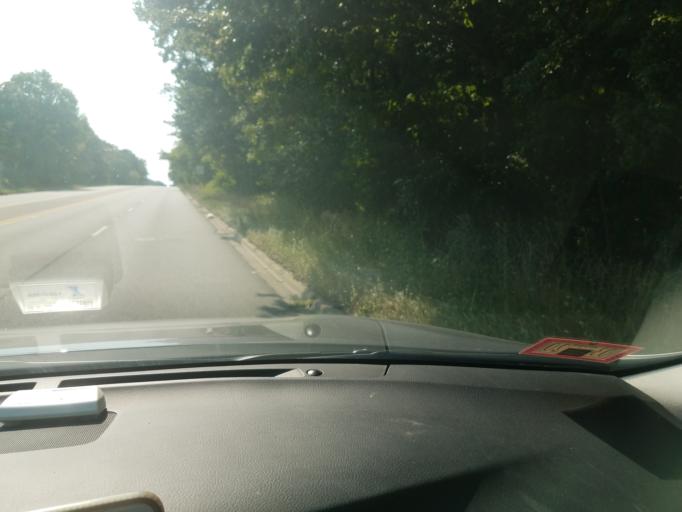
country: US
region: Illinois
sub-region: Cook County
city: Northbrook
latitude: 42.1382
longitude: -87.8169
